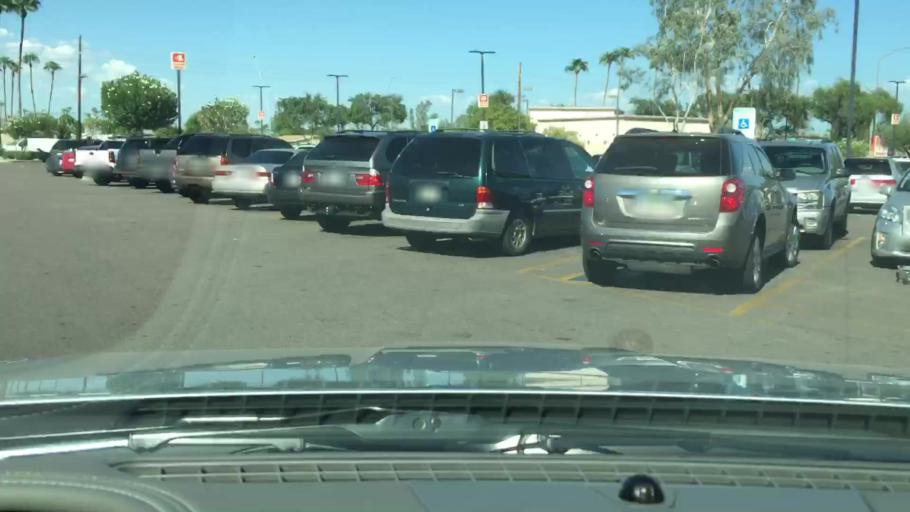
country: US
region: Arizona
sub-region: Maricopa County
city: Mesa
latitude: 33.4069
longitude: -111.7724
